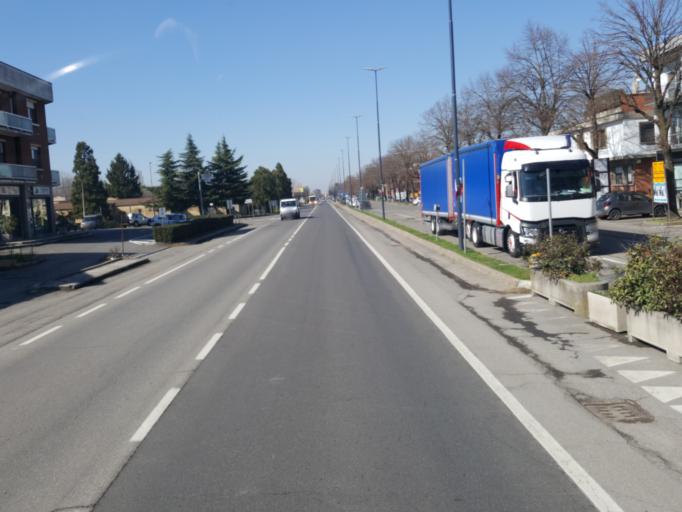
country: IT
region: Emilia-Romagna
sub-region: Provincia di Piacenza
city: Roveleto
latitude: 44.9665
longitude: 9.8502
